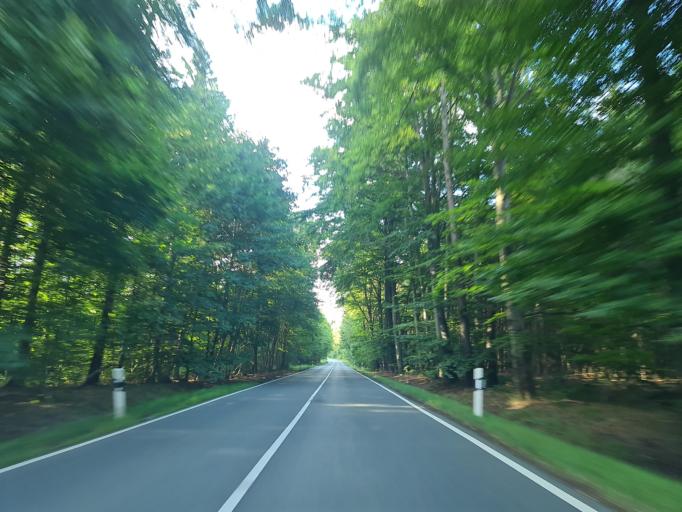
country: DE
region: Saxony
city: Pausa
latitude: 50.6031
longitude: 11.9974
